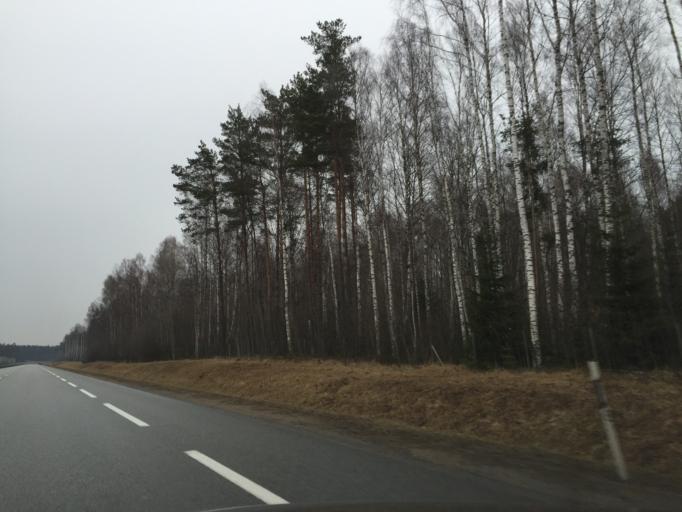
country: LV
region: Saulkrastu
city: Saulkrasti
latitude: 57.2528
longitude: 24.4288
